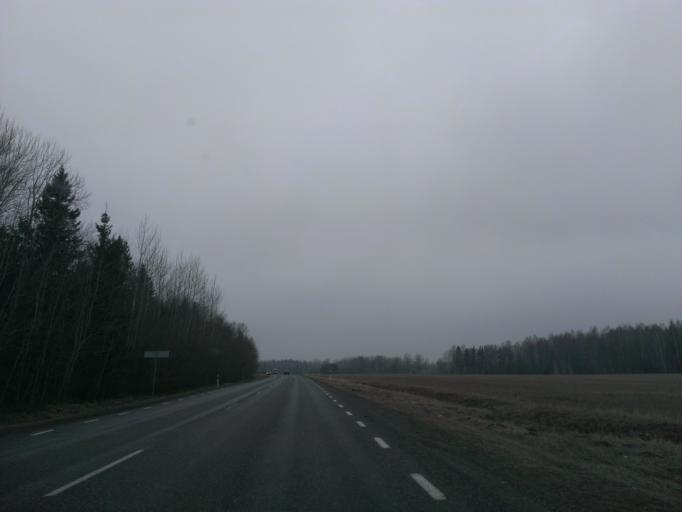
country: EE
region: Paernumaa
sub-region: Audru vald
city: Audru
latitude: 58.4776
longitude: 24.1785
